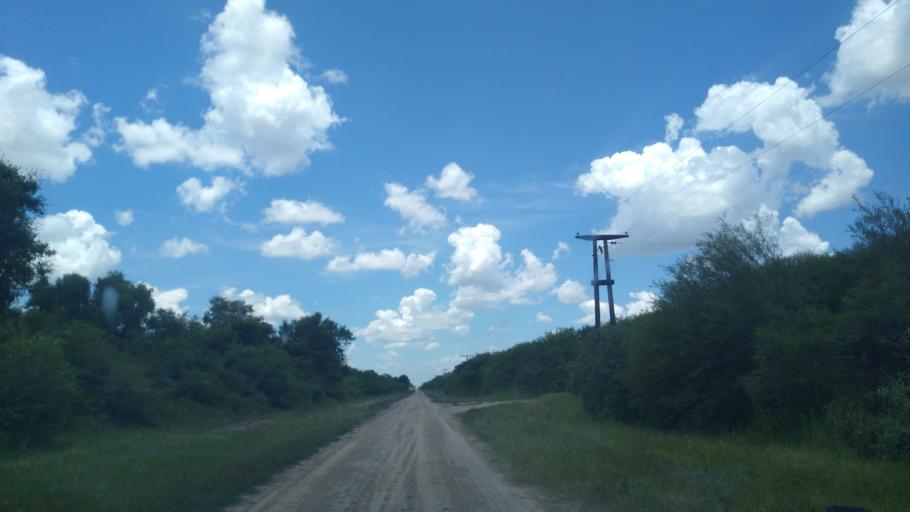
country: AR
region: Chaco
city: Presidencia Roque Saenz Pena
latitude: -26.7479
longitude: -60.3365
